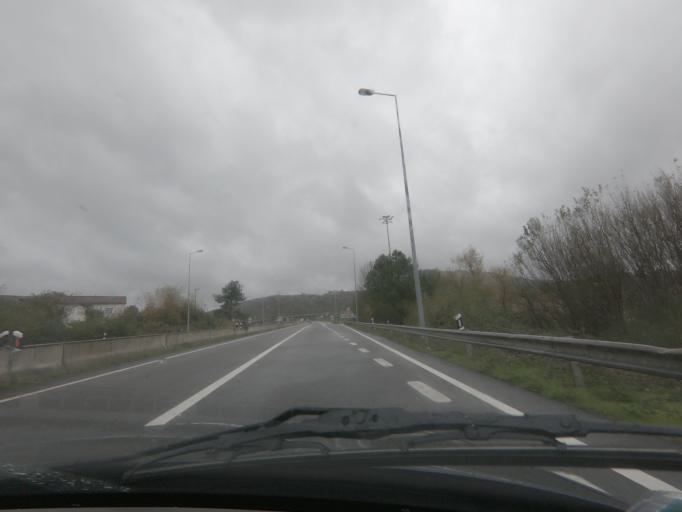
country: PT
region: Vila Real
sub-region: Vila Real
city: Vila Real
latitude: 41.2831
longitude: -7.8032
